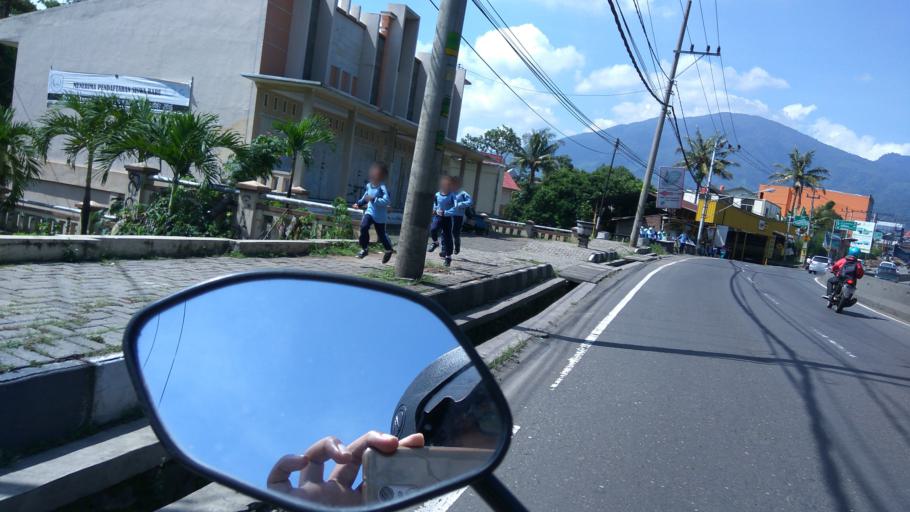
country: ID
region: Central Java
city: Ungaran
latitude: -7.1206
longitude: 110.4102
